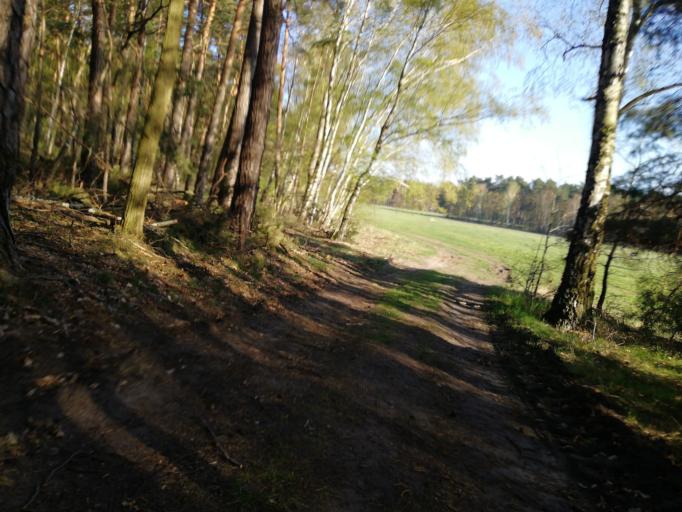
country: DE
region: Brandenburg
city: Calau
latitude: 51.7193
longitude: 13.9593
